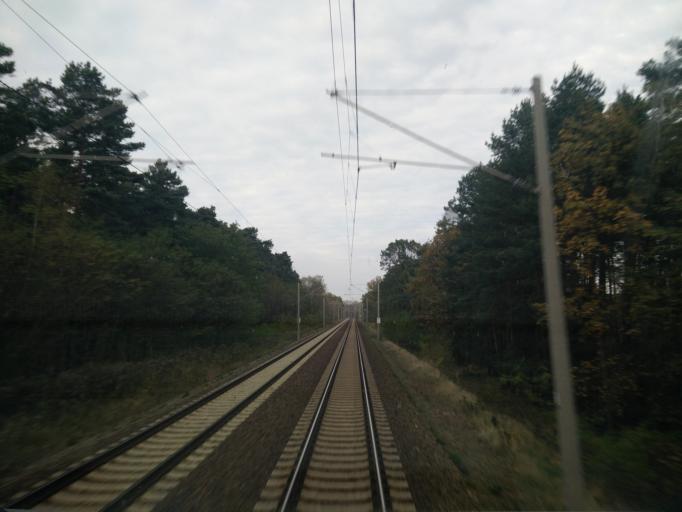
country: DE
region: Brandenburg
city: Halbe
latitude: 52.0479
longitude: 13.7202
